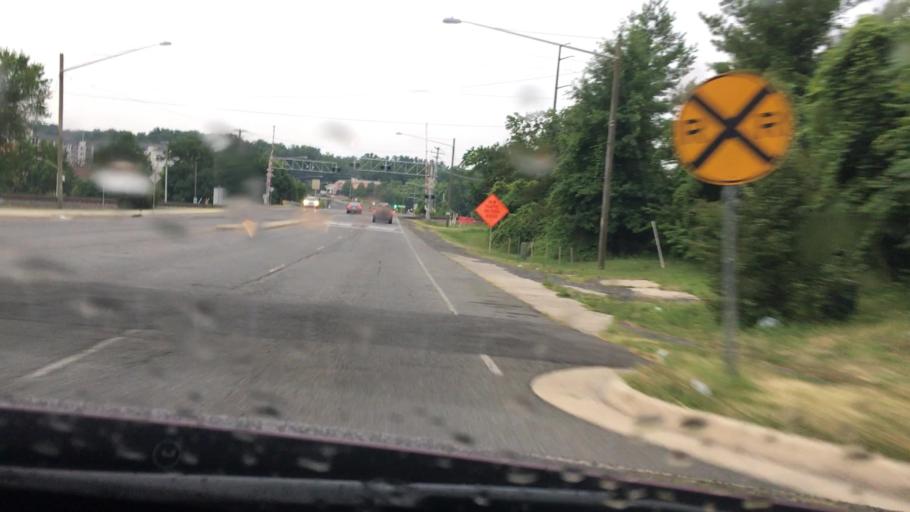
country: US
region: Virginia
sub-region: Prince William County
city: Yorkshire
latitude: 38.7655
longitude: -77.4424
